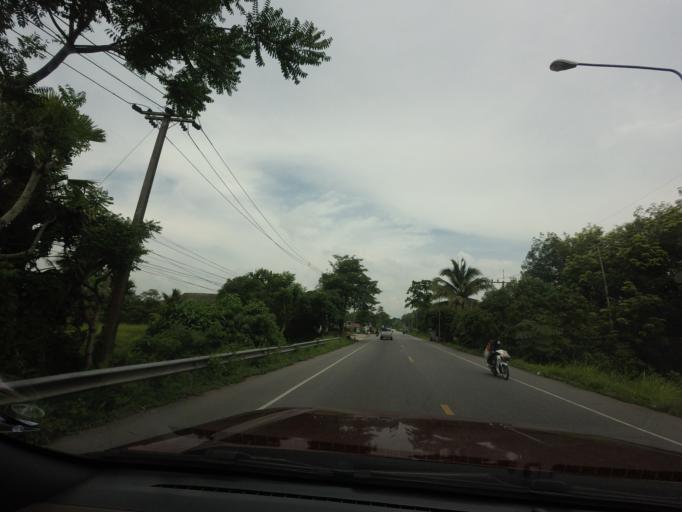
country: TH
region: Yala
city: Yala
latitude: 6.6075
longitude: 101.3051
